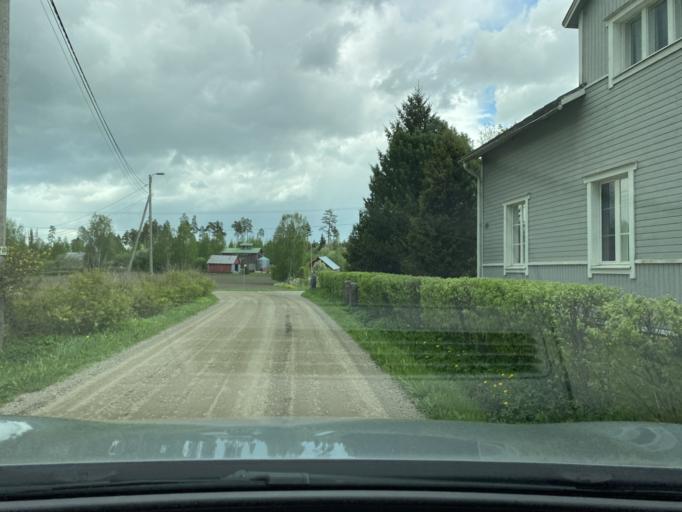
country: FI
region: Uusimaa
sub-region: Porvoo
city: Pukkila
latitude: 60.7638
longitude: 25.4339
